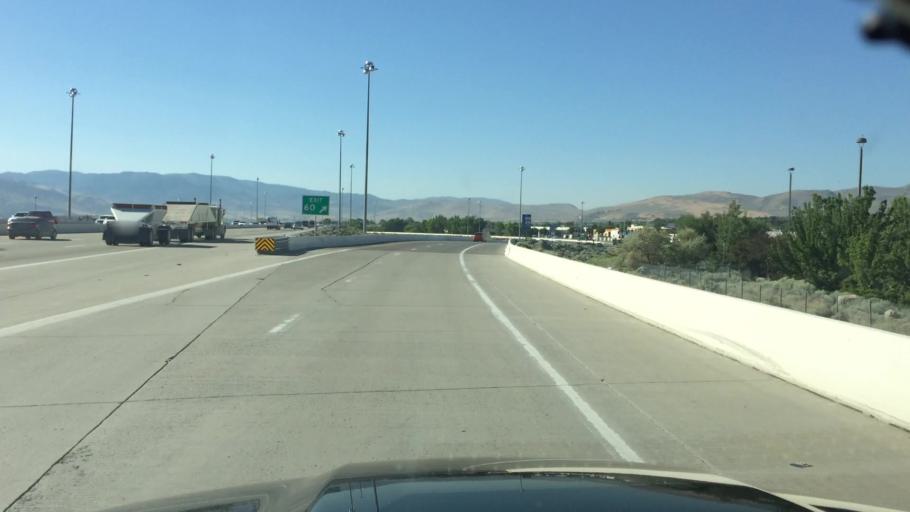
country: US
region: Nevada
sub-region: Washoe County
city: Sparks
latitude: 39.4425
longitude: -119.7673
